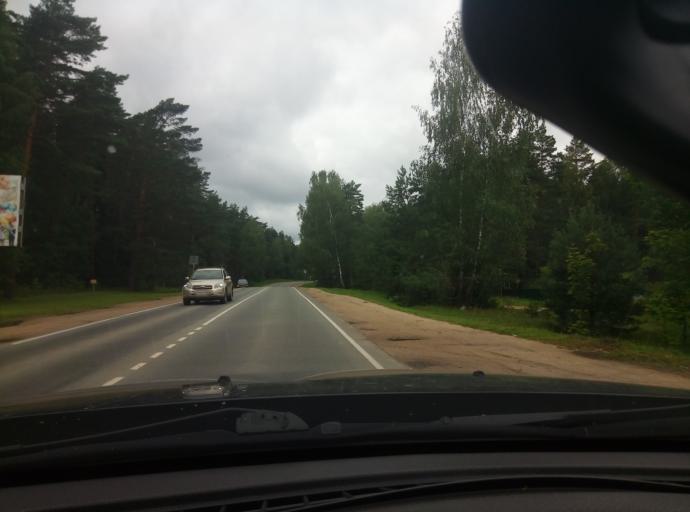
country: RU
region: Kaluga
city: Zhukovo
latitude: 55.0409
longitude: 36.7284
